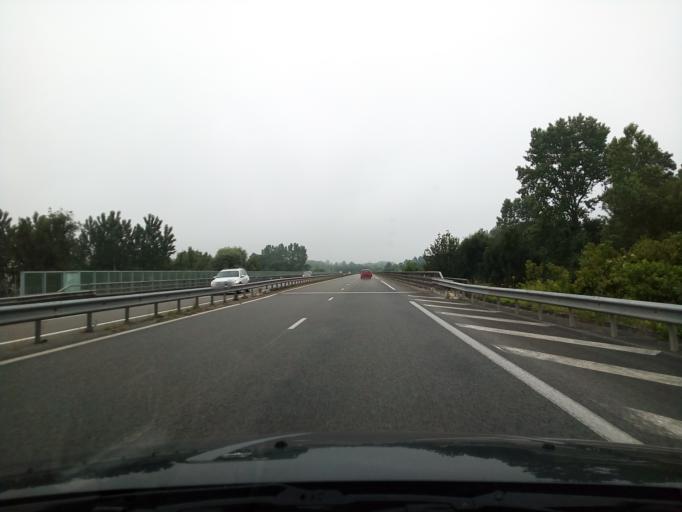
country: FR
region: Poitou-Charentes
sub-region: Departement de la Charente
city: Jarnac
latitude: 45.6736
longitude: -0.1586
